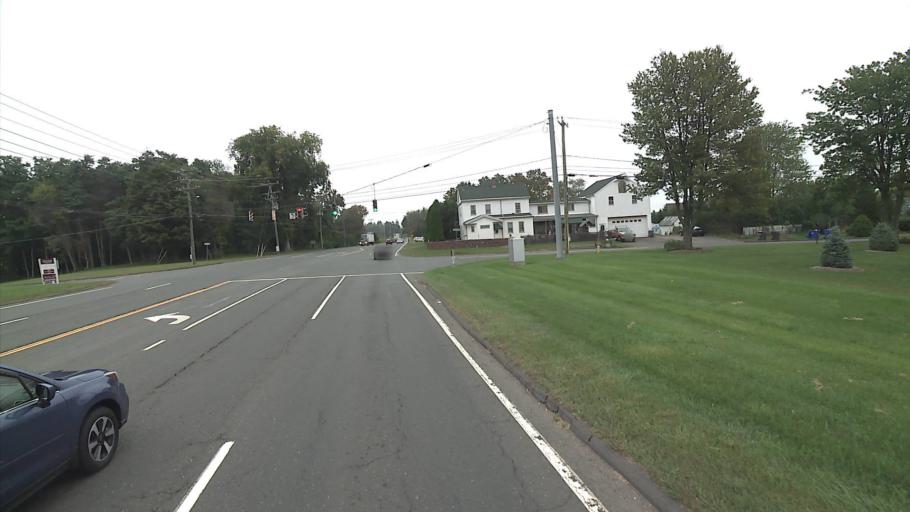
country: US
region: Connecticut
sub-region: Hartford County
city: Suffield Depot
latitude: 41.9620
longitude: -72.6625
